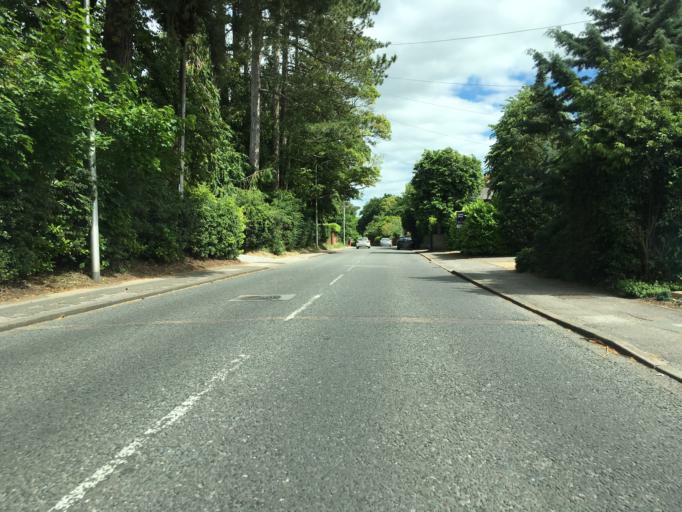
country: GB
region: England
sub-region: West Berkshire
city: Newbury
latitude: 51.3836
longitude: -1.3383
